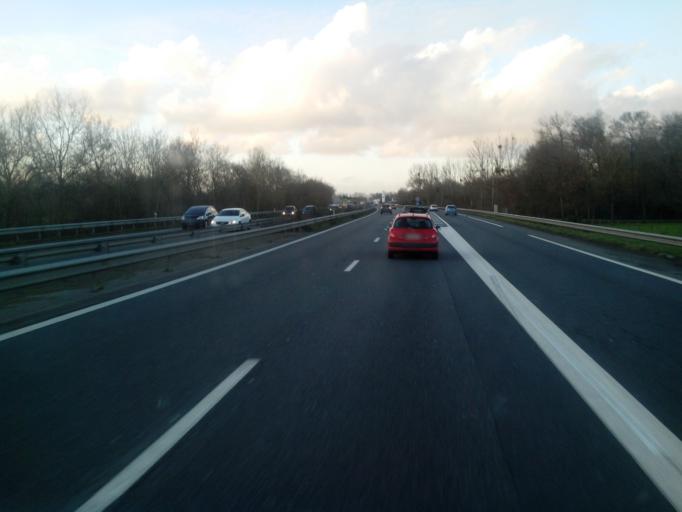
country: FR
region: Pays de la Loire
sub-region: Departement de la Loire-Atlantique
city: Basse-Goulaine
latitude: 47.2227
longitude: -1.4586
